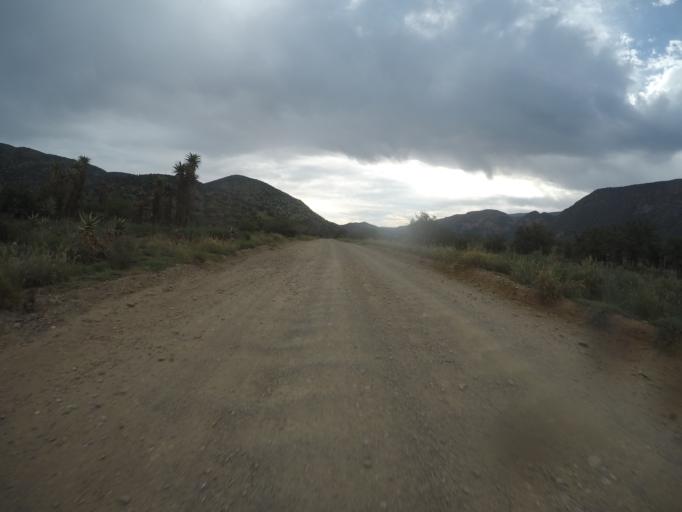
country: ZA
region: Eastern Cape
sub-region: Cacadu District Municipality
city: Willowmore
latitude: -33.5268
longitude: 23.8575
